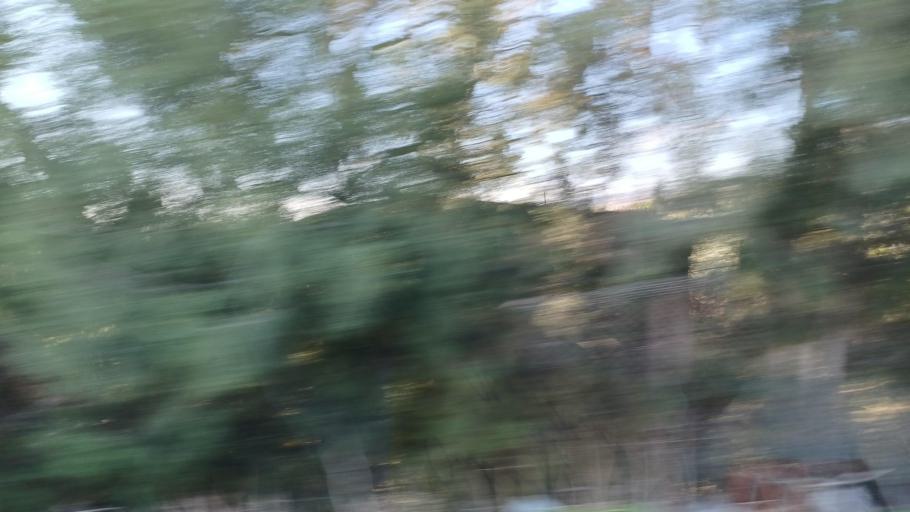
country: CY
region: Larnaka
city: Psevdas
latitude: 34.9380
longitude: 33.5260
